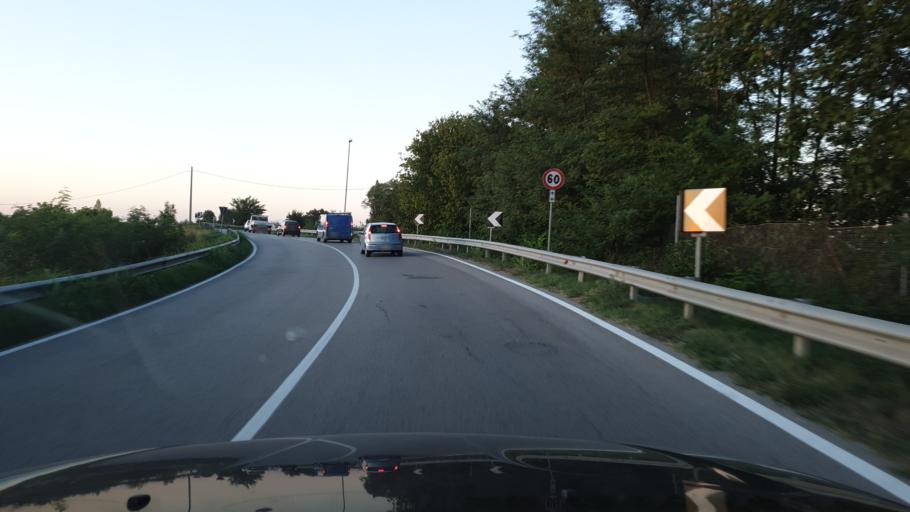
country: IT
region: Emilia-Romagna
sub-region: Provincia di Bologna
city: Ca De Fabbri
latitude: 44.5981
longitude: 11.4381
